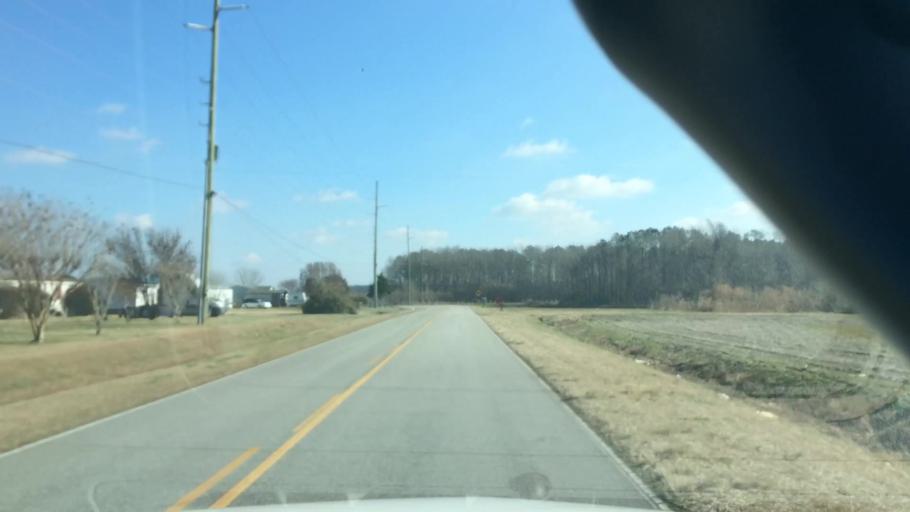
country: US
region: North Carolina
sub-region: Pitt County
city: Grifton
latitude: 35.4191
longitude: -77.4283
